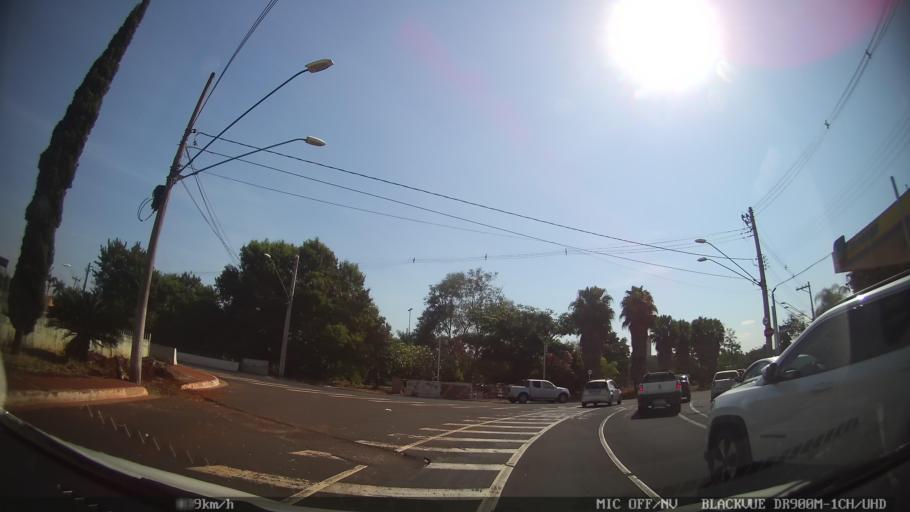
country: BR
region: Sao Paulo
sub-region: Ribeirao Preto
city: Ribeirao Preto
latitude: -21.1674
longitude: -47.8138
